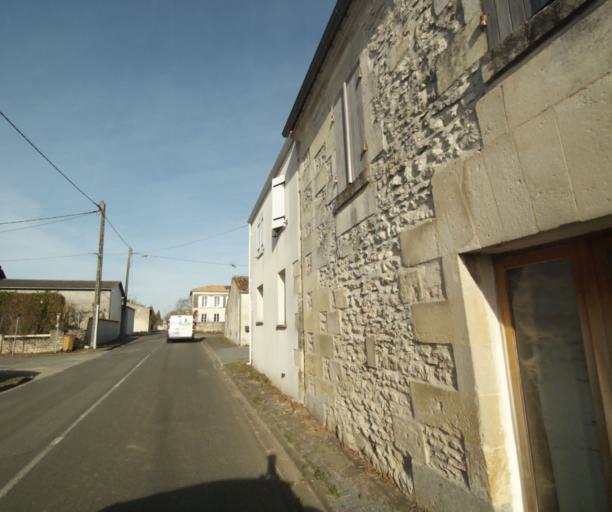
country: FR
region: Poitou-Charentes
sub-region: Departement de la Charente-Maritime
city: Chaniers
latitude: 45.7315
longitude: -0.5579
